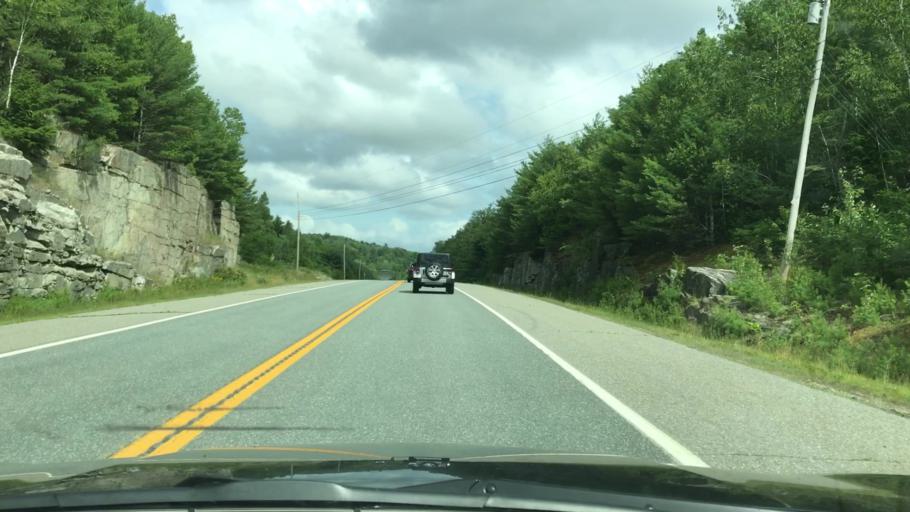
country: US
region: Maine
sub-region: Hancock County
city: Surry
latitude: 44.5643
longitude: -68.6004
